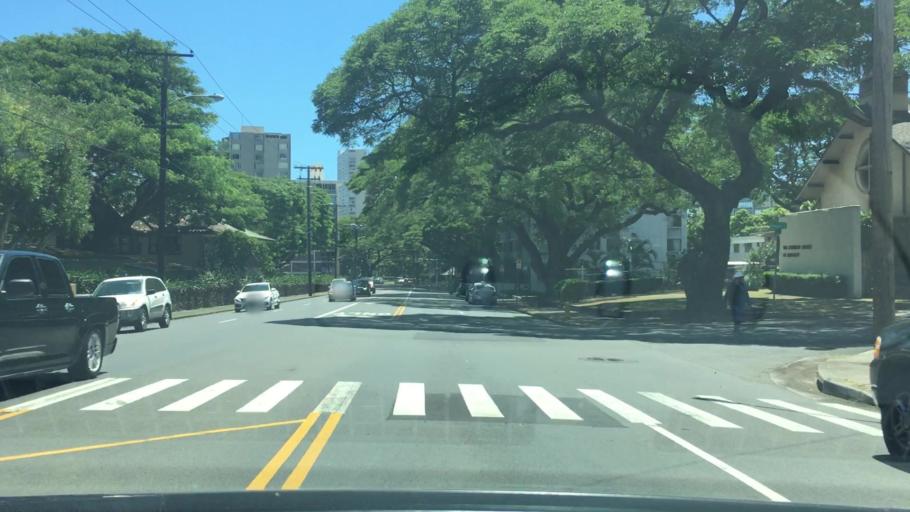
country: US
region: Hawaii
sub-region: Honolulu County
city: Honolulu
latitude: 21.3042
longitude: -157.8312
